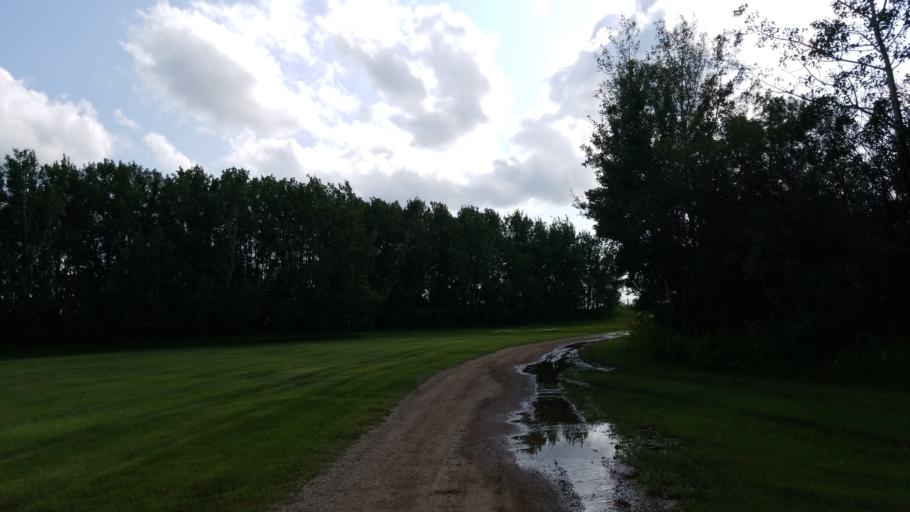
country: CA
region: Saskatchewan
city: Lloydminster
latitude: 53.2568
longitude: -110.0443
